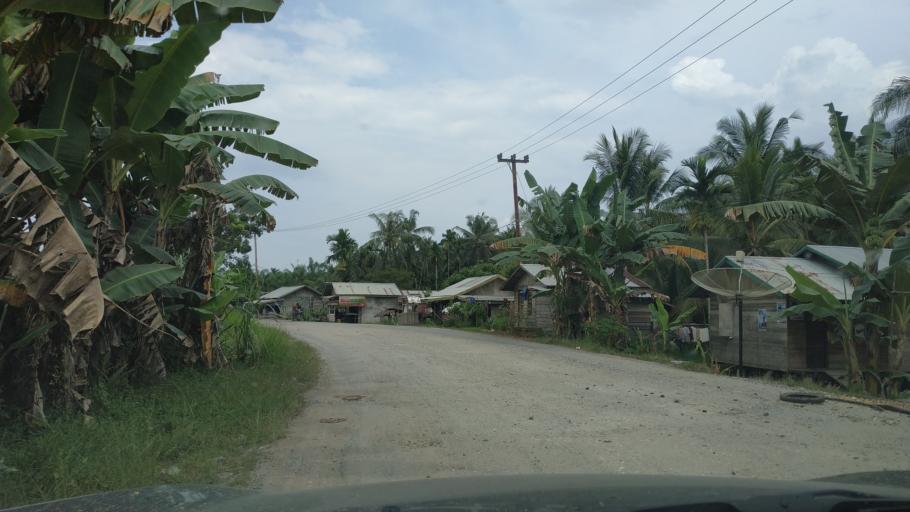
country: ID
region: Riau
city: Sungaisalak
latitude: -0.5181
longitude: 103.0038
